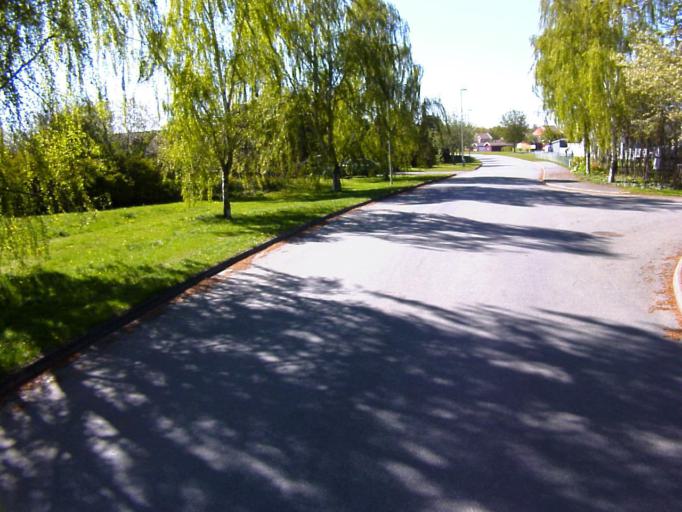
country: SE
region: Skane
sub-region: Kristianstads Kommun
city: Kristianstad
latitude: 56.0303
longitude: 14.1979
